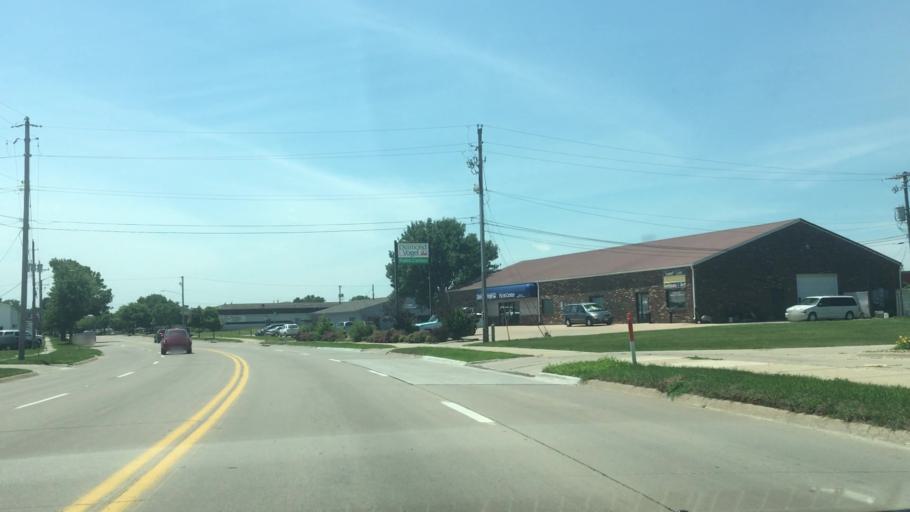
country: US
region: Iowa
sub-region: Johnson County
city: Iowa City
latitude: 41.6438
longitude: -91.5334
